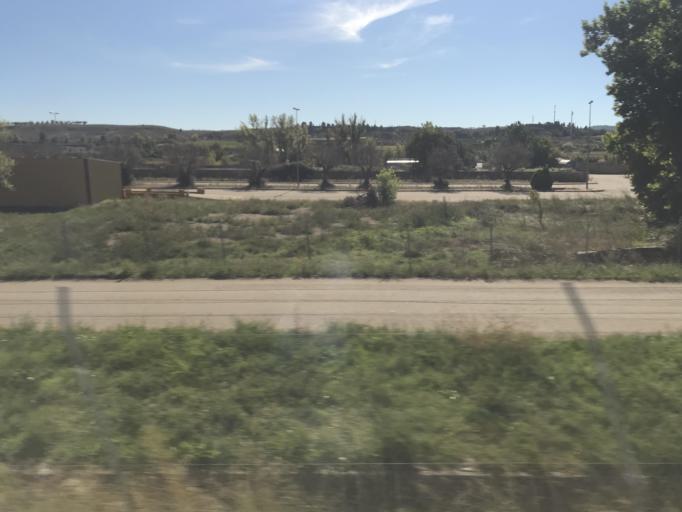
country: ES
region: Aragon
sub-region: Provincia de Zaragoza
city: Terrer
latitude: 41.3230
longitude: -1.7030
